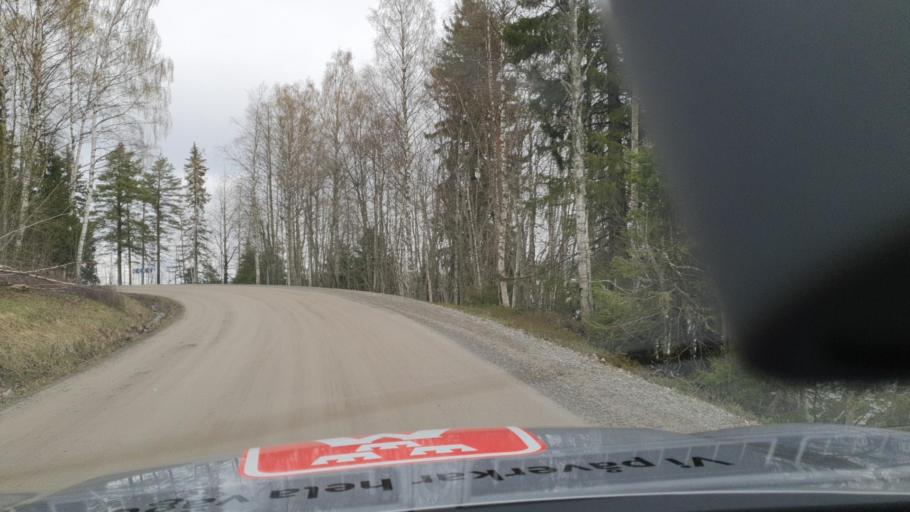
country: SE
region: Vaesternorrland
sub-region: OErnskoeldsviks Kommun
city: Husum
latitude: 63.6323
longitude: 19.0599
